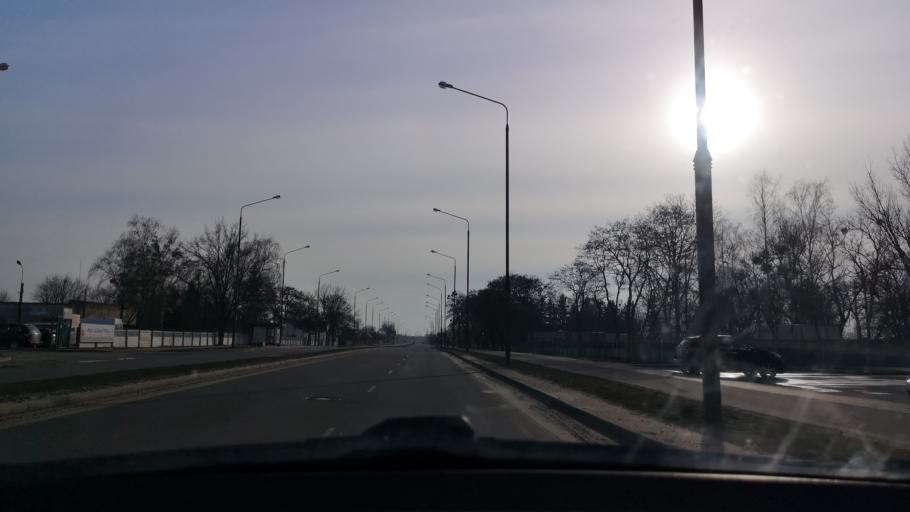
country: BY
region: Brest
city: Brest
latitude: 52.1195
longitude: 23.6703
